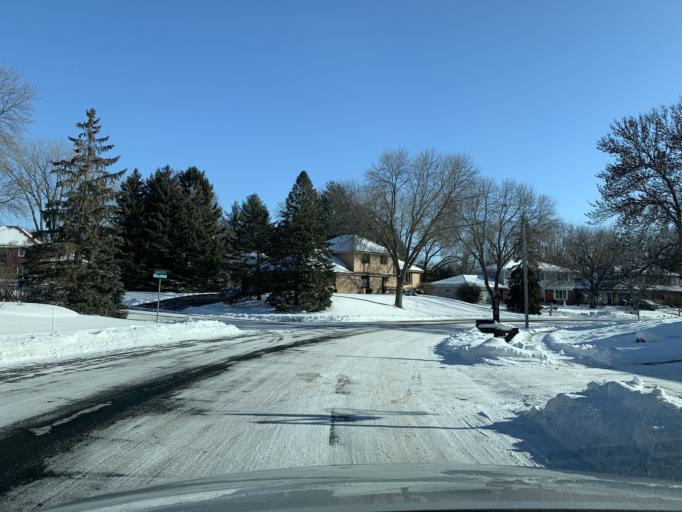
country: US
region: Minnesota
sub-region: Hennepin County
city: Edina
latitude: 44.8359
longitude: -93.3572
